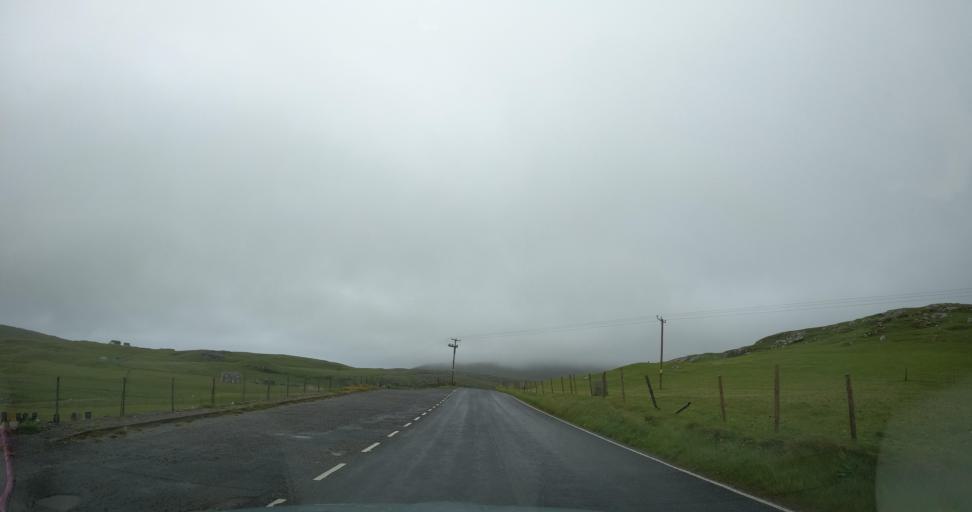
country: GB
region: Scotland
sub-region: Eilean Siar
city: Barra
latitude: 57.0023
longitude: -7.5002
